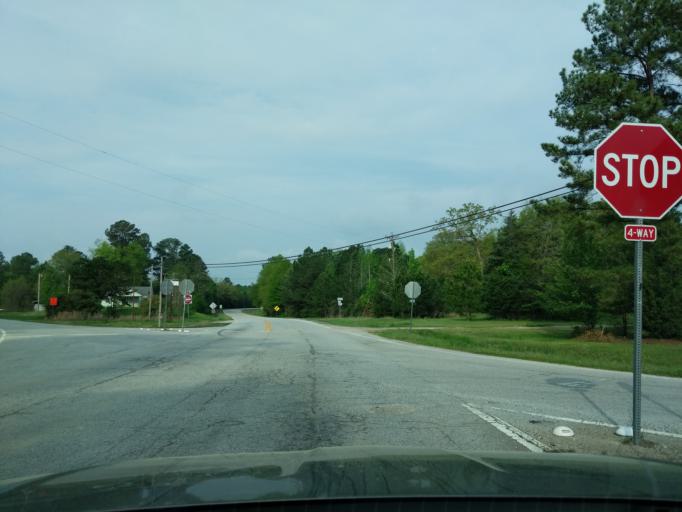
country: US
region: Georgia
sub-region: Lincoln County
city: Lincolnton
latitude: 33.8059
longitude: -82.3965
